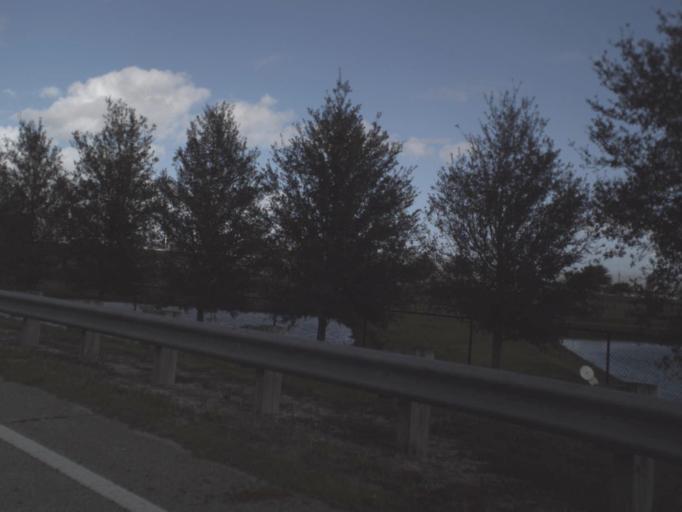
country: US
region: Florida
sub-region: Volusia County
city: Daytona Beach
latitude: 29.1765
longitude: -81.0767
